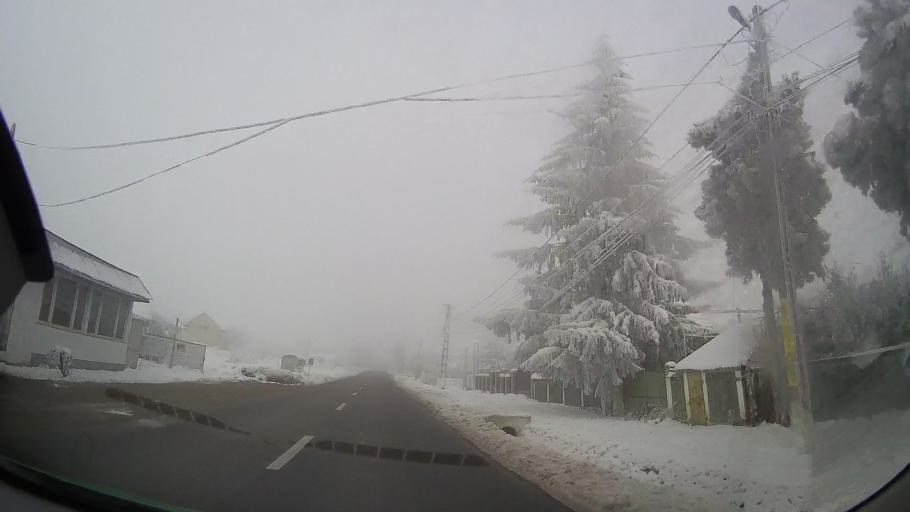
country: RO
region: Iasi
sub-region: Comuna Mircesti
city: Mircesti
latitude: 47.0924
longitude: 26.8211
